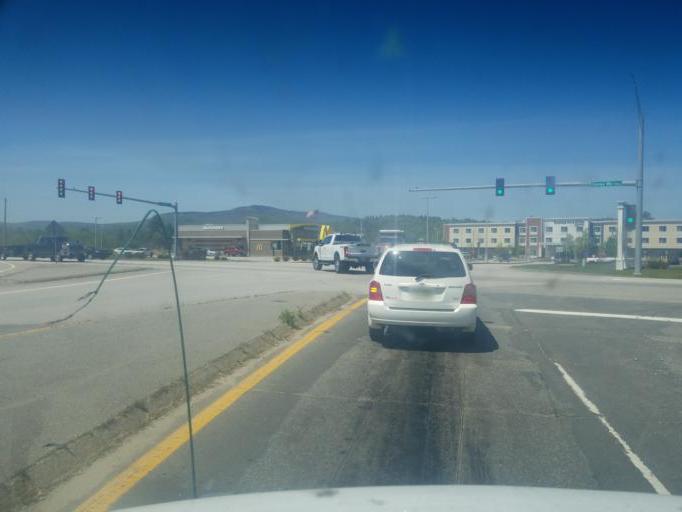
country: US
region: New Hampshire
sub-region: Grafton County
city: Plymouth
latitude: 43.7706
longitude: -71.7218
